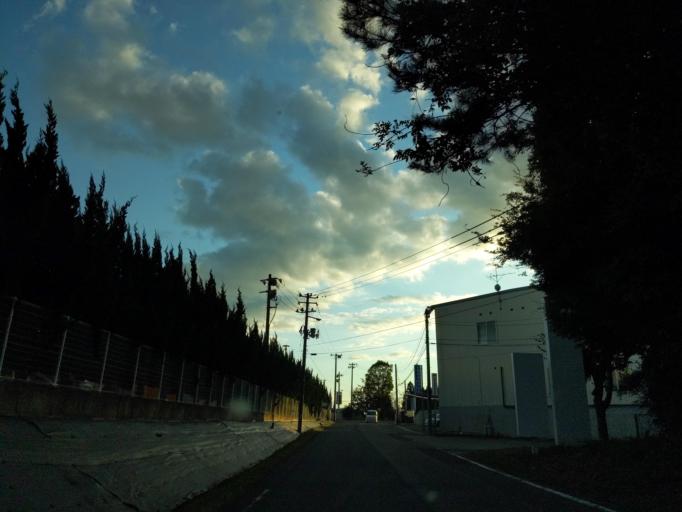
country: JP
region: Fukushima
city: Motomiya
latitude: 37.4762
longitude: 140.4294
